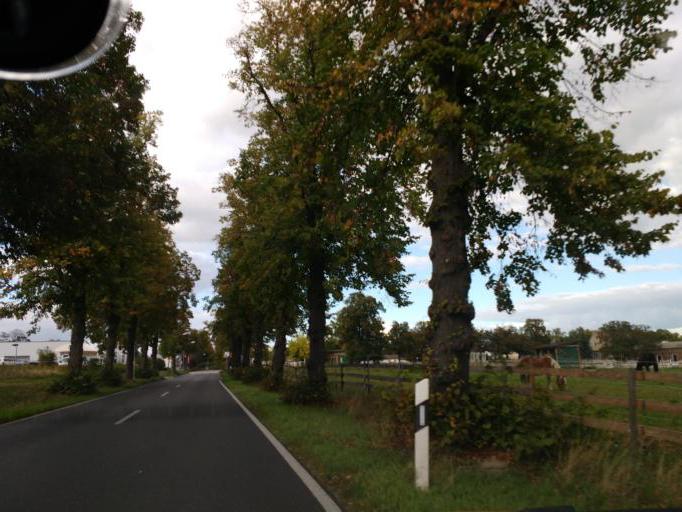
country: DE
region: Berlin
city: Lichtenrade
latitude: 52.3926
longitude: 13.4431
